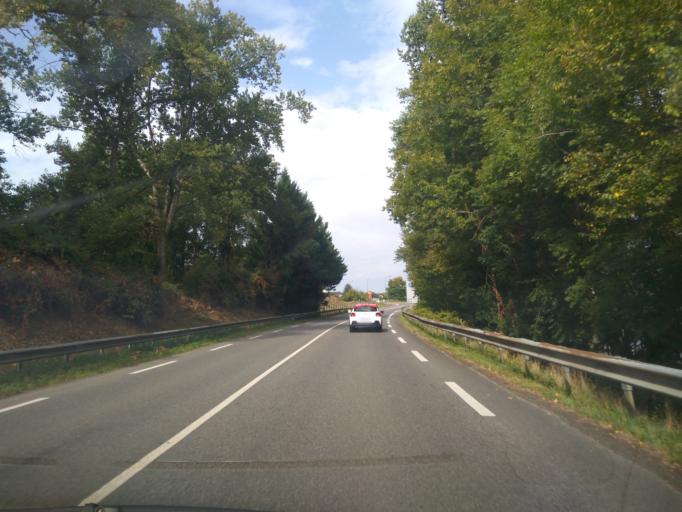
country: FR
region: Aquitaine
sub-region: Departement des Pyrenees-Atlantiques
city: Artiguelouve
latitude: 43.3076
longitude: -0.4453
